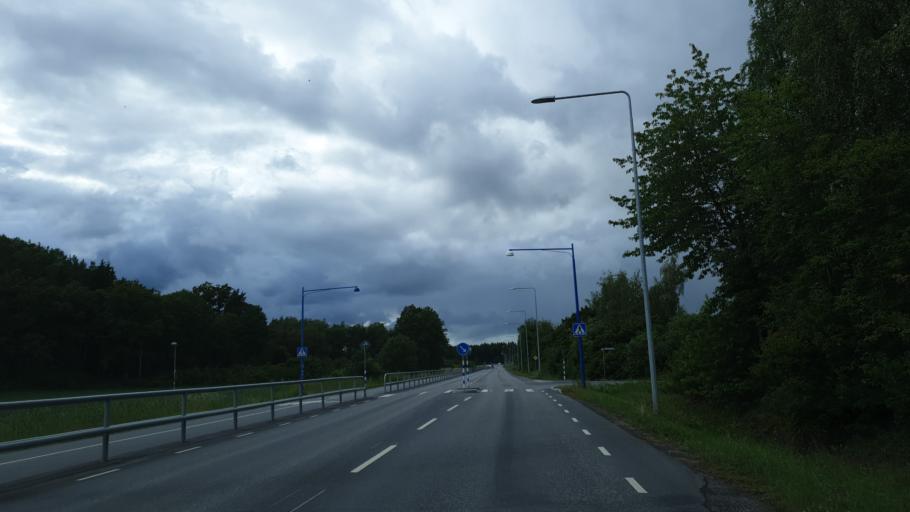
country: SE
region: Stockholm
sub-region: Jarfalla Kommun
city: Jakobsberg
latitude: 59.4208
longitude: 17.8117
